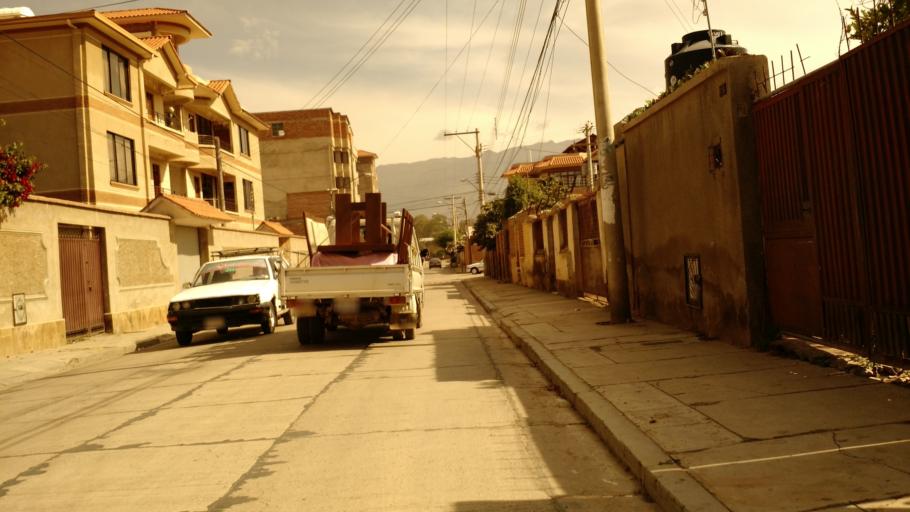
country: BO
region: Cochabamba
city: Cochabamba
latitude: -17.4242
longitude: -66.1597
